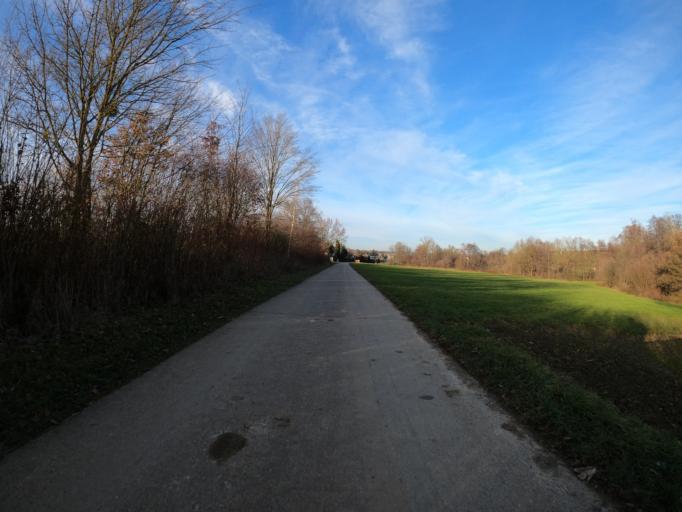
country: DE
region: Baden-Wuerttemberg
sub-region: Regierungsbezirk Stuttgart
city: Hattenhofen
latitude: 48.6613
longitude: 9.5792
